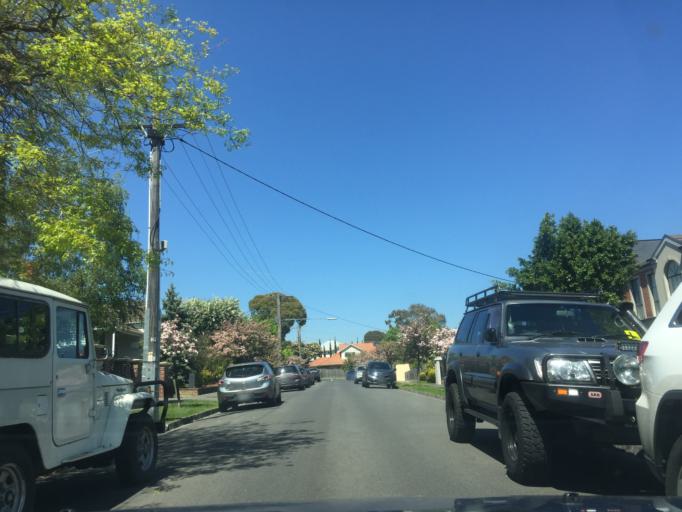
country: AU
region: Victoria
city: Mont Albert
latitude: -37.8166
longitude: 145.0907
